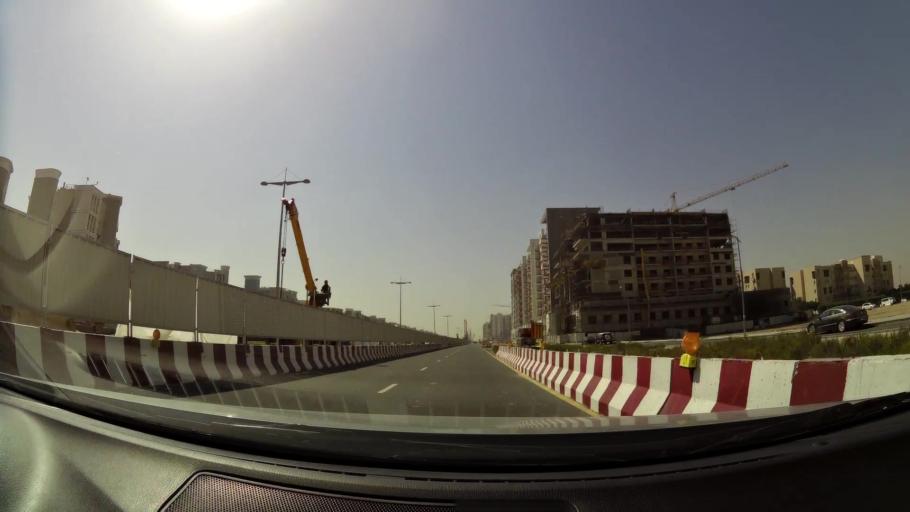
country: AE
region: Dubai
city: Dubai
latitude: 25.0334
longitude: 55.1480
